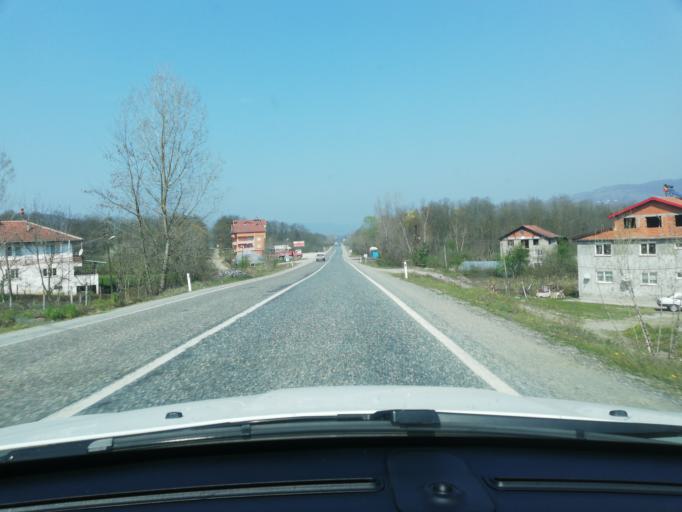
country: TR
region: Zonguldak
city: Gokcebey
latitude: 41.2904
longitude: 32.1377
